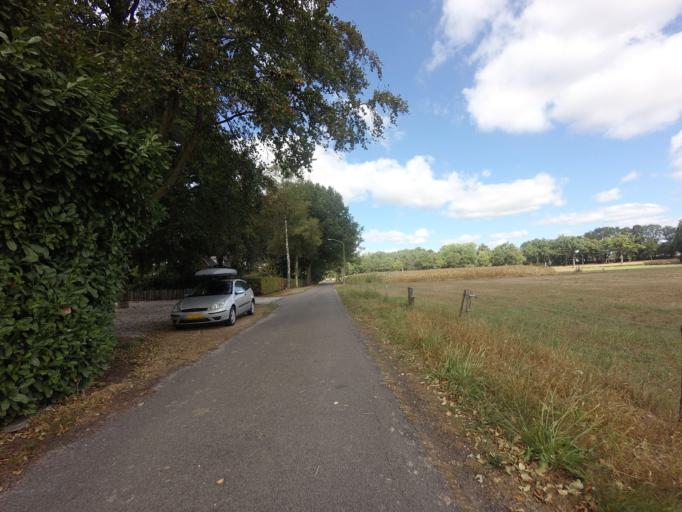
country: NL
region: North Brabant
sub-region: Gemeente Landerd
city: Schaijk
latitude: 51.7355
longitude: 5.6294
